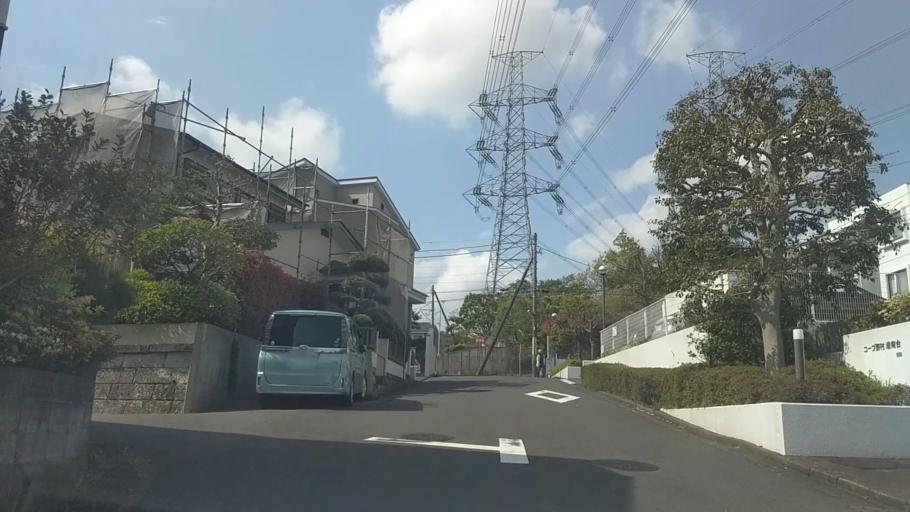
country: JP
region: Kanagawa
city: Kamakura
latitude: 35.3787
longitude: 139.5672
